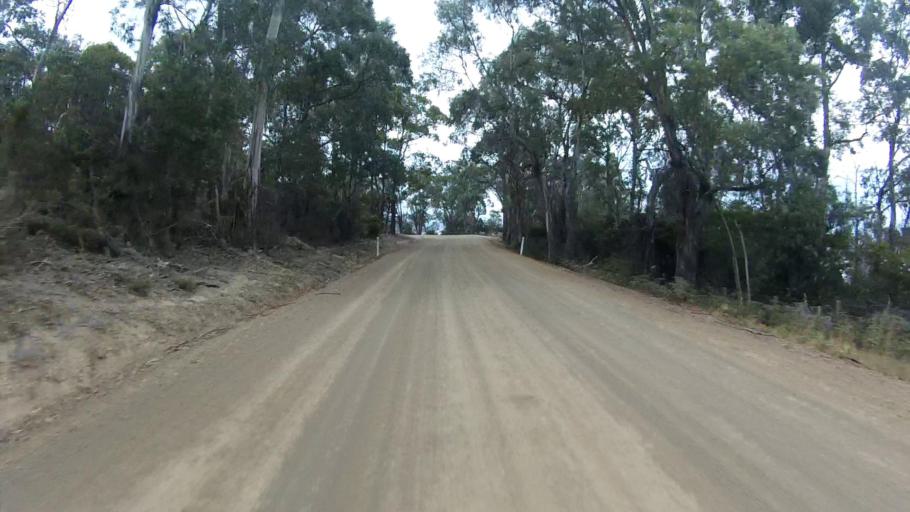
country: AU
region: Tasmania
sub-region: Huon Valley
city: Cygnet
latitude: -43.2238
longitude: 147.0938
